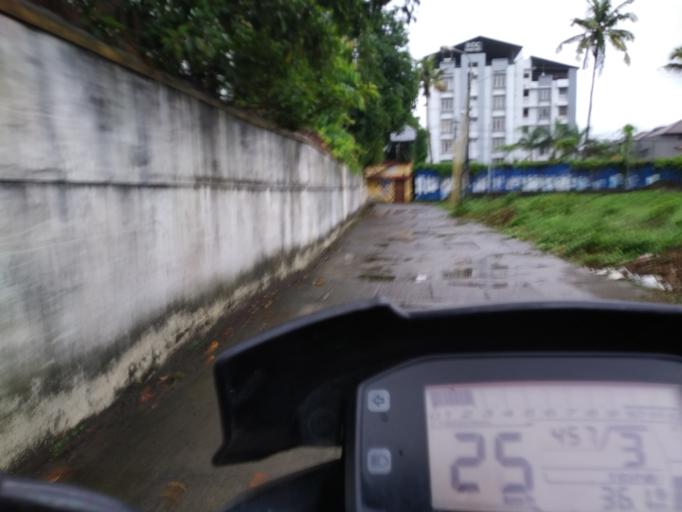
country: IN
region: Kerala
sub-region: Ernakulam
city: Cochin
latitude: 9.9771
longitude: 76.3077
